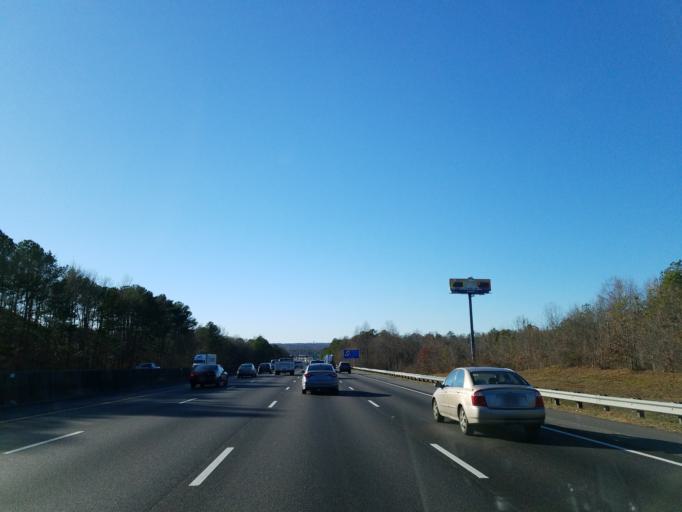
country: US
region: Georgia
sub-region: Cobb County
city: Mableton
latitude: 33.7761
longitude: -84.5911
